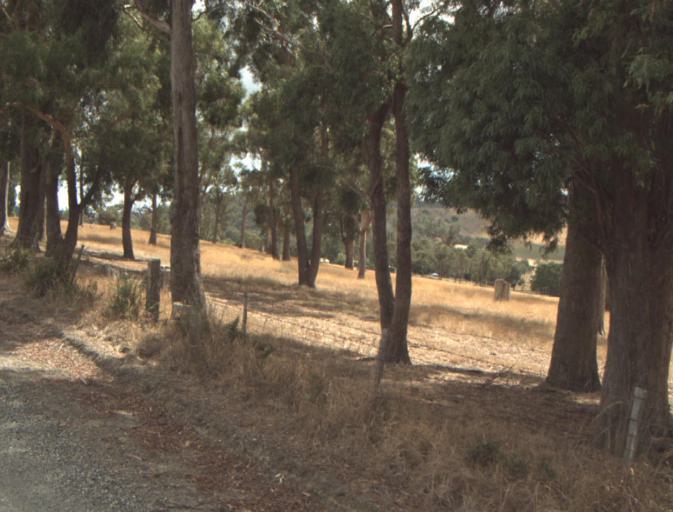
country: AU
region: Tasmania
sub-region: Launceston
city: Mayfield
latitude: -41.2190
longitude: 147.1421
